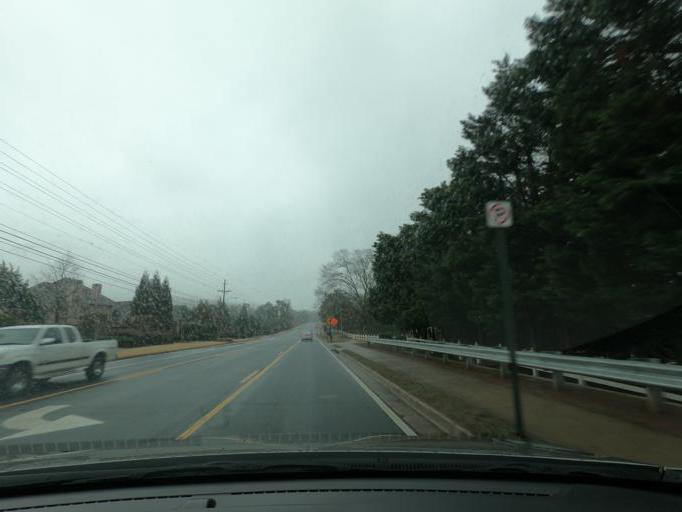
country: US
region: Georgia
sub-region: Cherokee County
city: Woodstock
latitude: 34.0721
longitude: -84.4790
